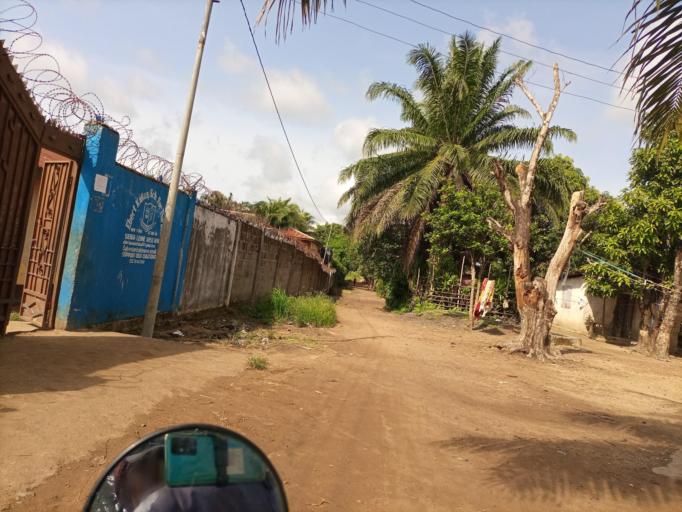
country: SL
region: Southern Province
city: Bo
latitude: 7.9636
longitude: -11.7642
